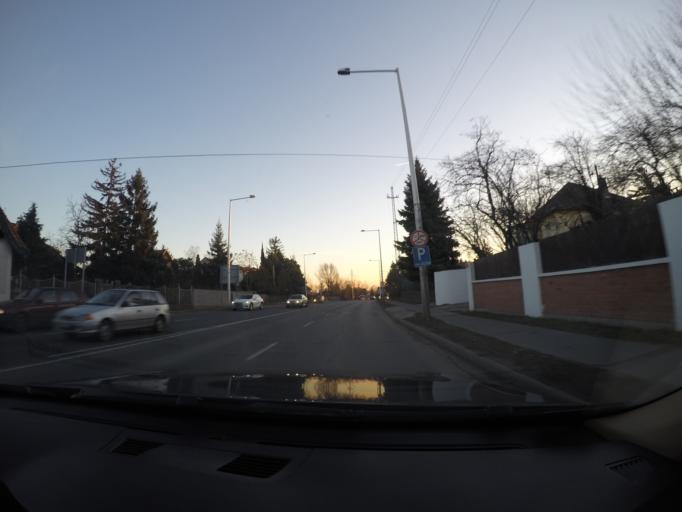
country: HU
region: Pest
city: Szentendre
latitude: 47.6726
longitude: 19.0727
